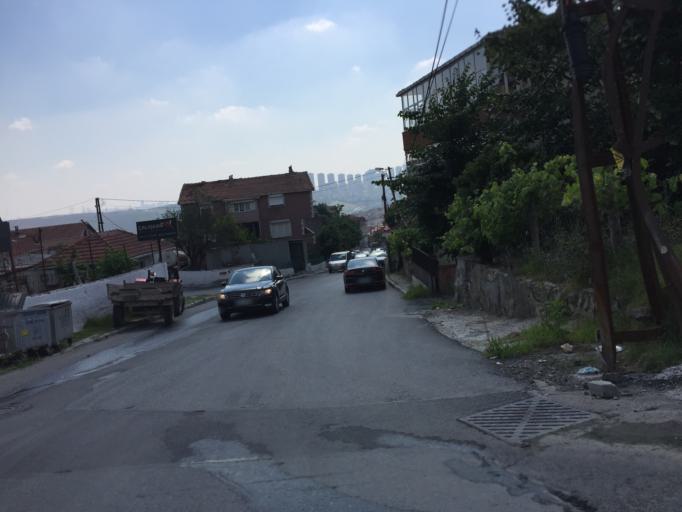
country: TR
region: Istanbul
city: Esenyurt
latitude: 41.0836
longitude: 28.6571
